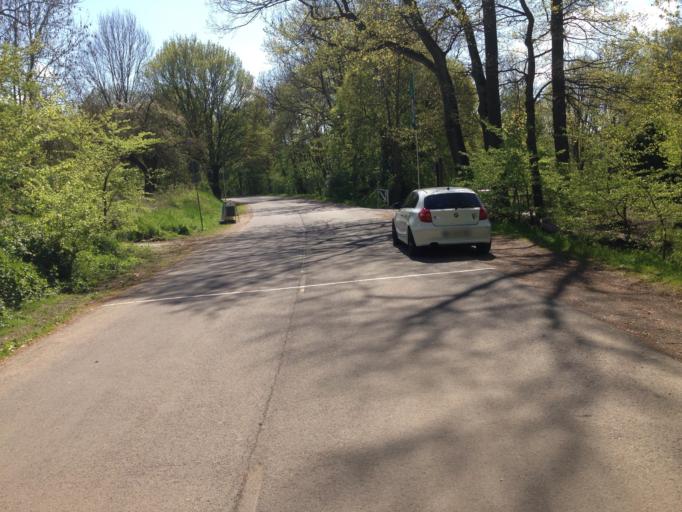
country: DE
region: Hesse
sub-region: Regierungsbezirk Giessen
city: Lich
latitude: 50.5305
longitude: 8.8146
